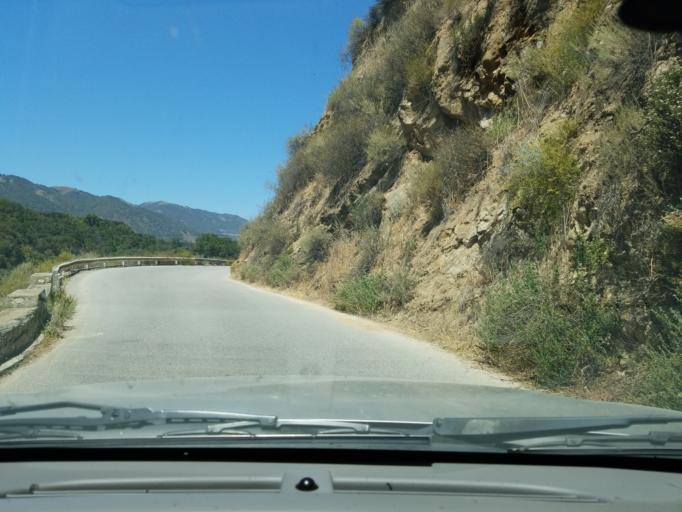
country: US
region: California
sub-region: Monterey County
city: Carmel Valley Village
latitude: 36.4695
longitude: -121.7131
